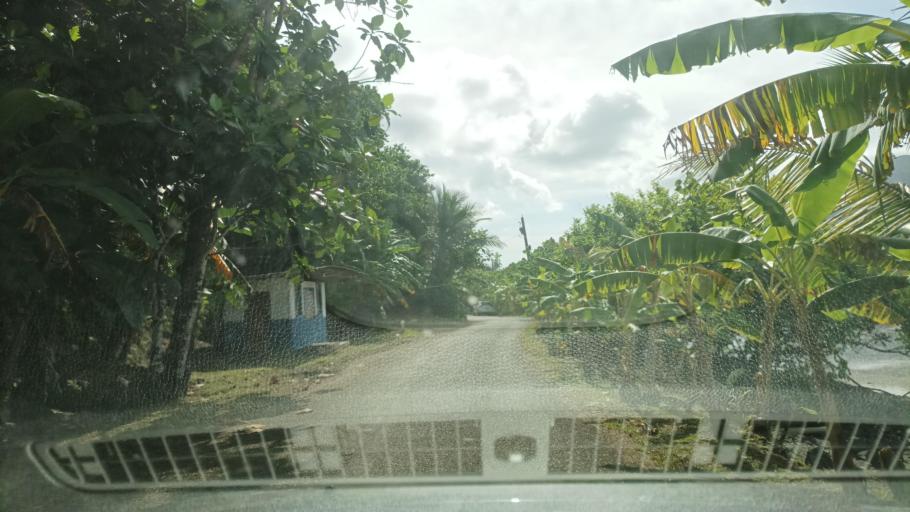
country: FM
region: Kosrae
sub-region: Lelu Municipality
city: Lelu
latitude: 5.3336
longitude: 163.0304
